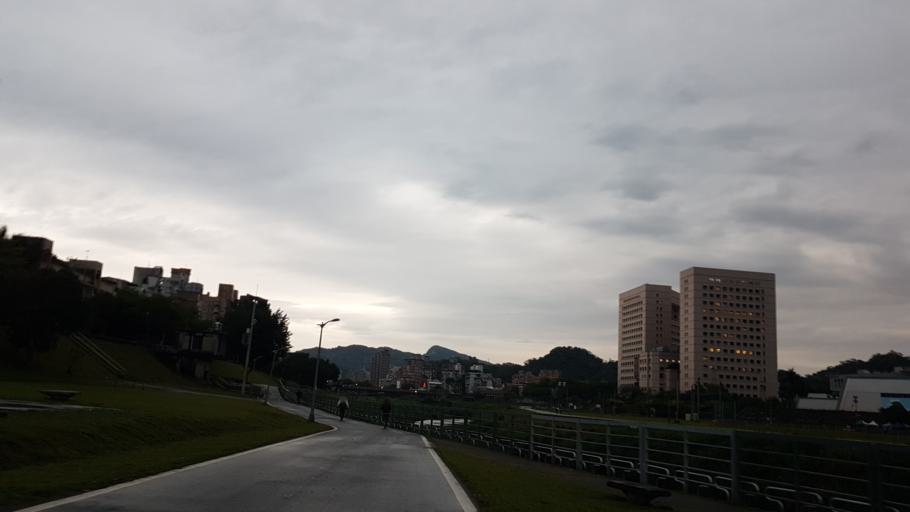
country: TW
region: Taipei
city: Taipei
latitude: 24.9833
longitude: 121.5713
